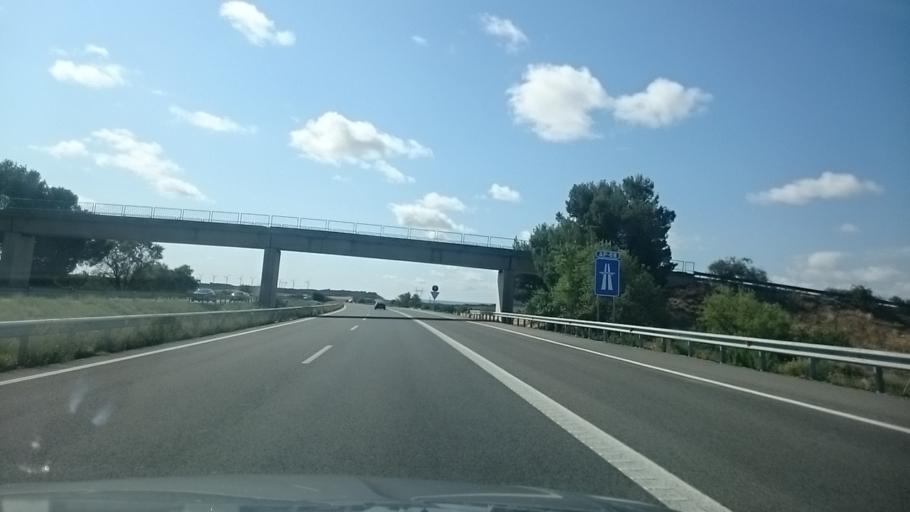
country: ES
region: Navarre
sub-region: Provincia de Navarra
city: Corella
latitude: 42.1143
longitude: -1.7367
